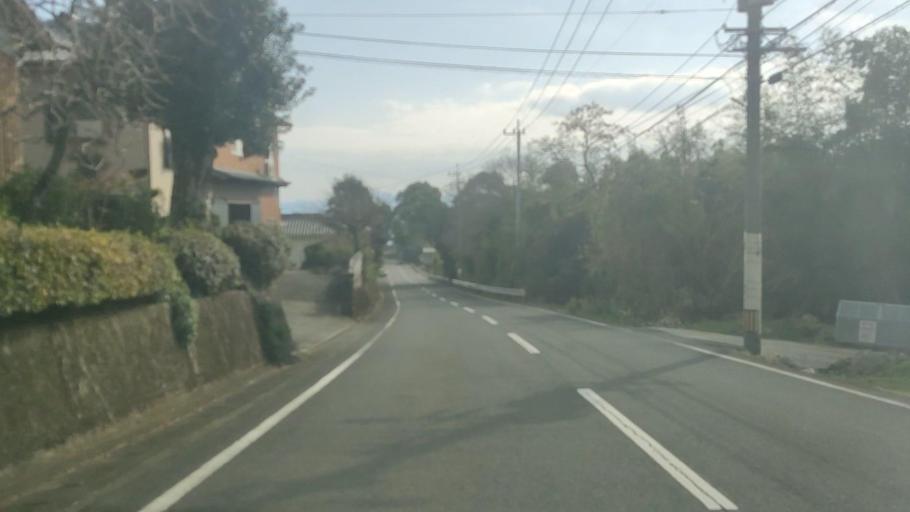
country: JP
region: Nagasaki
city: Shimabara
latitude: 32.6680
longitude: 130.2861
